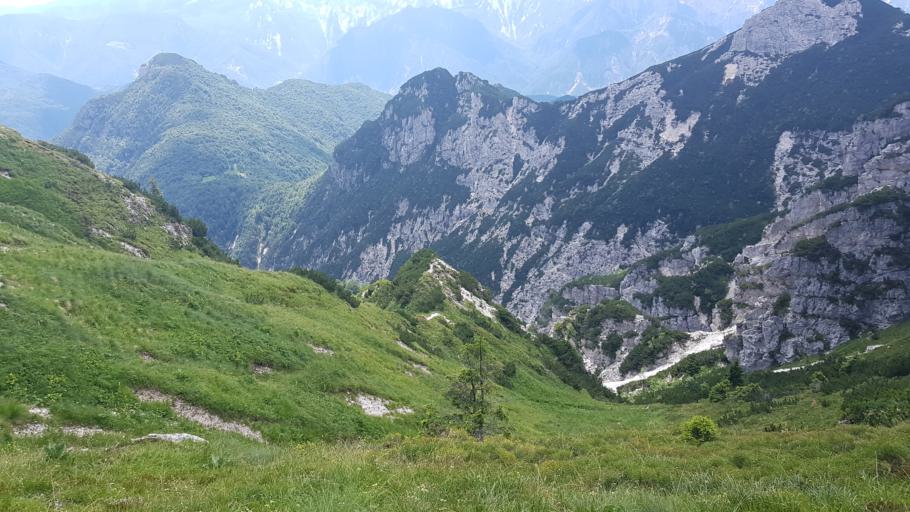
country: IT
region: Friuli Venezia Giulia
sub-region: Provincia di Udine
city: Dogna
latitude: 46.4432
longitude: 13.2783
